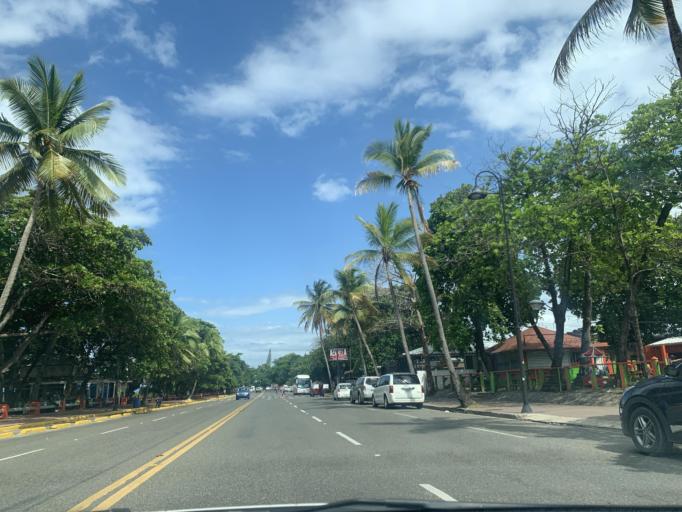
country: DO
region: Puerto Plata
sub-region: Puerto Plata
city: Puerto Plata
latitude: 19.7918
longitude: -70.6748
